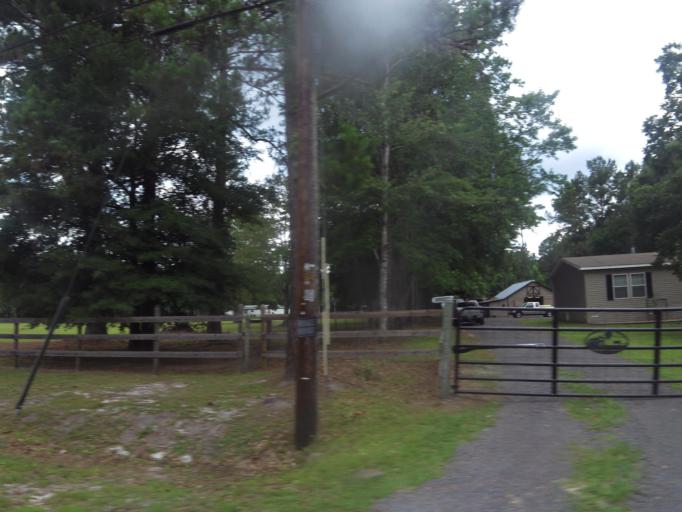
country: US
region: Florida
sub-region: Duval County
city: Baldwin
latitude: 30.3389
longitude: -81.8780
